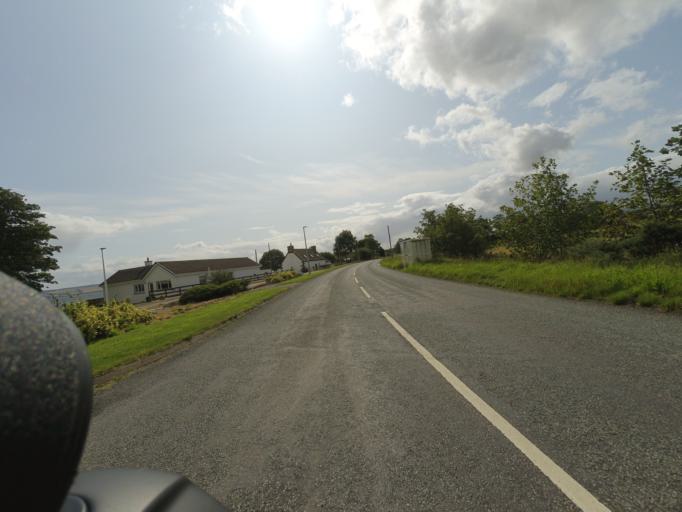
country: GB
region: Scotland
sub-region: Highland
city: Invergordon
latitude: 57.7250
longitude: -4.0973
